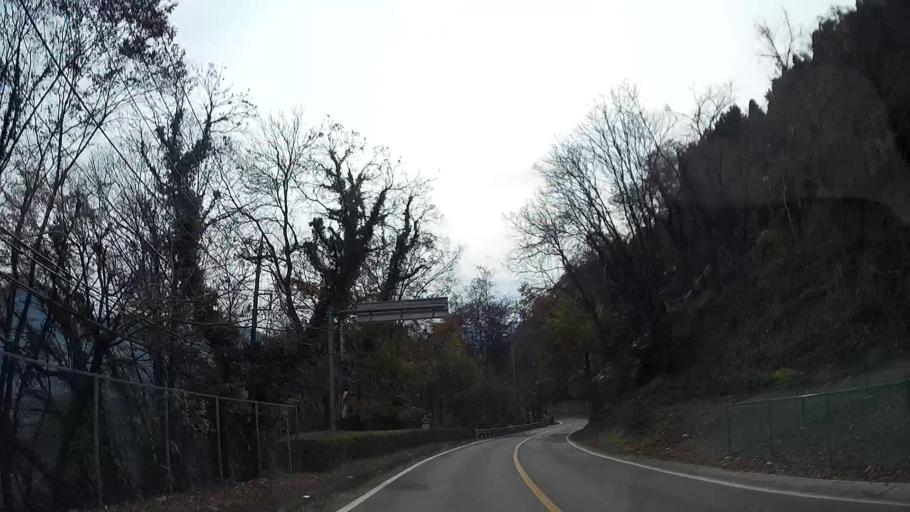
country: JP
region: Saitama
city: Chichibu
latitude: 35.9816
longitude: 139.0543
